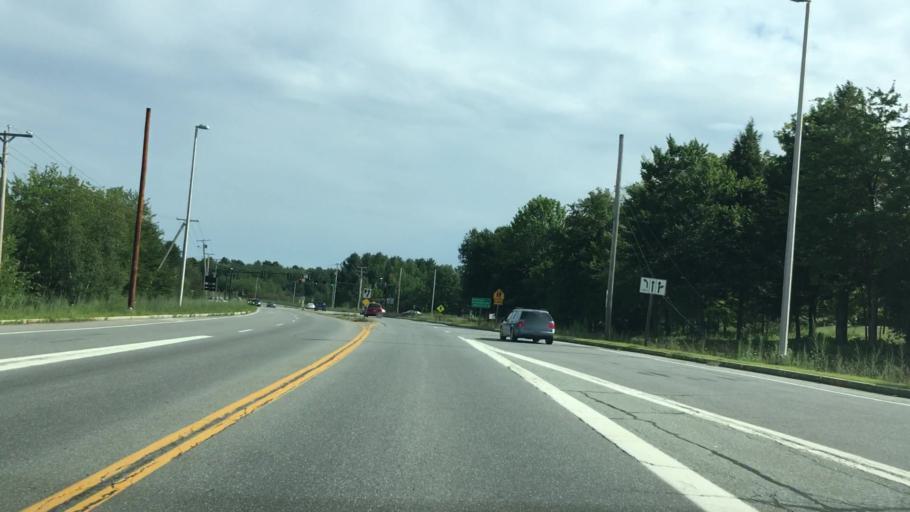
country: US
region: Maine
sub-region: Waldo County
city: Belfast
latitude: 44.4196
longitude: -69.0202
